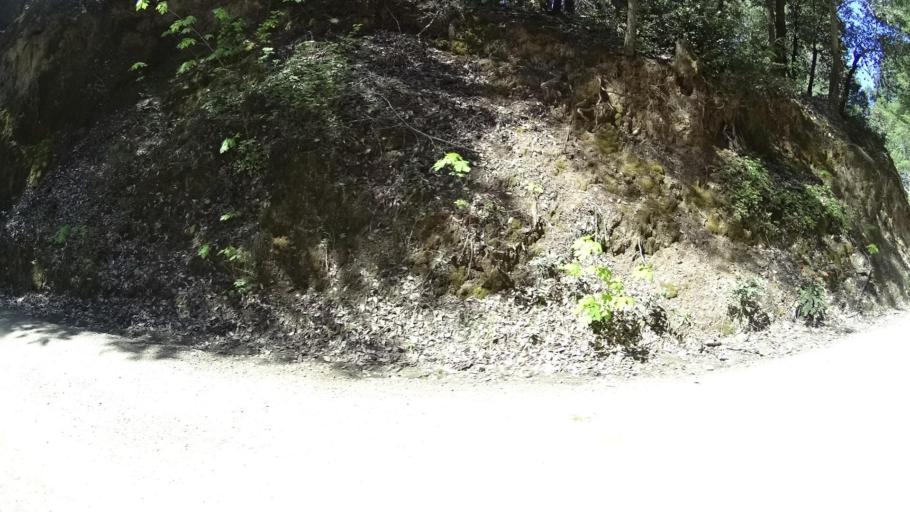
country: US
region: California
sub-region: Humboldt County
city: Rio Dell
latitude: 40.2166
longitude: -124.1076
